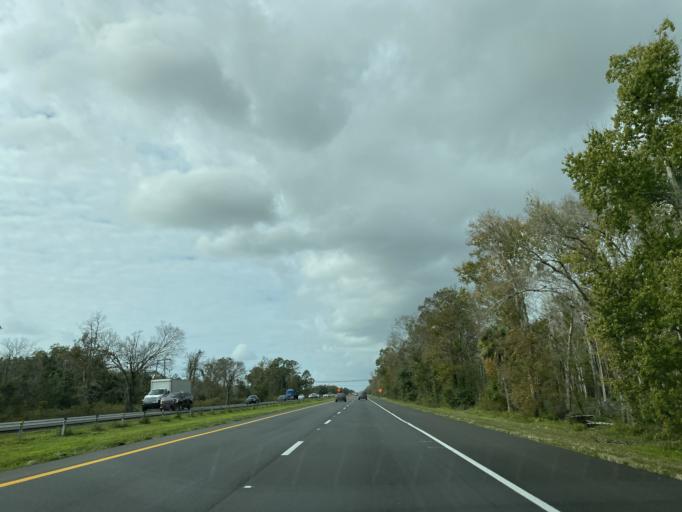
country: US
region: Florida
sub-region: Orange County
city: Wedgefield
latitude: 28.4526
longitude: -81.0038
